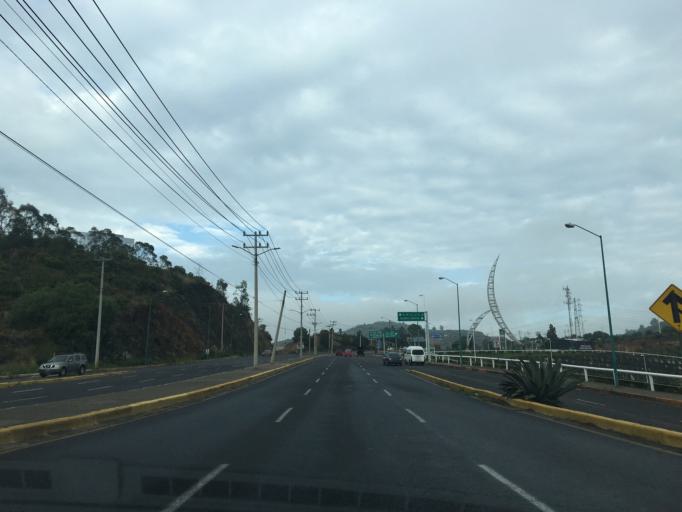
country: MX
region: Mexico
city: Ciudad Lopez Mateos
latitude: 19.5455
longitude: -99.2733
